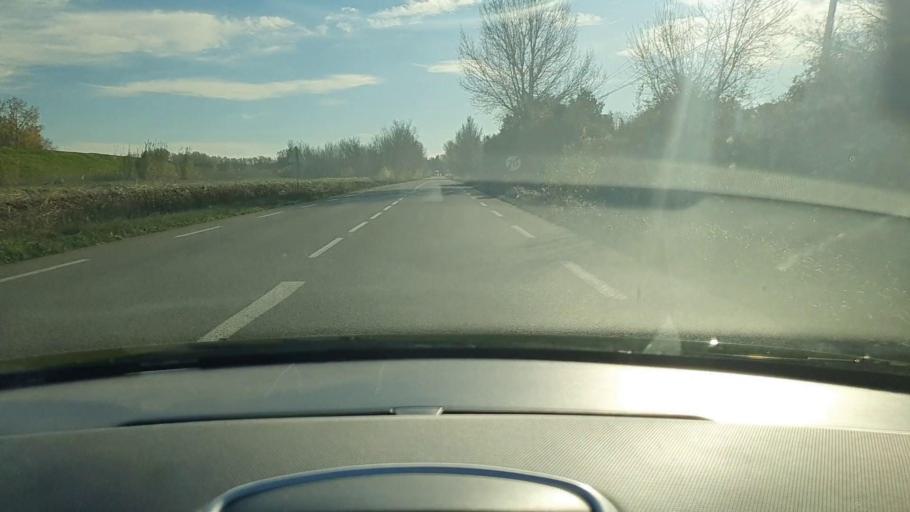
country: FR
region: Languedoc-Roussillon
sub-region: Departement du Gard
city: Fourques
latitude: 43.7027
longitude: 4.6016
